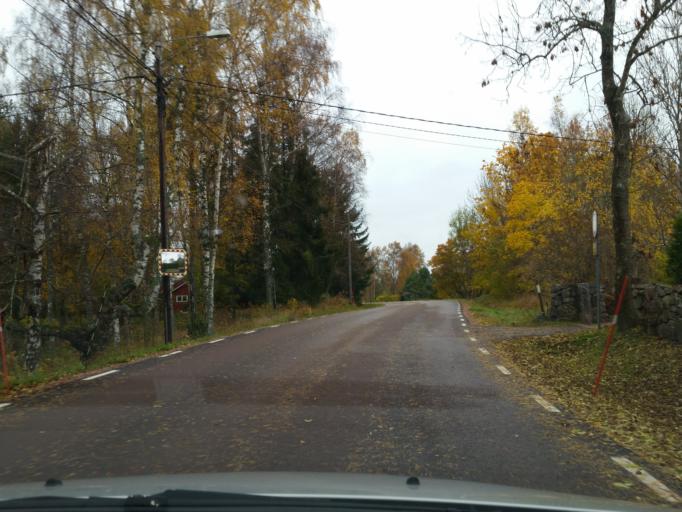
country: AX
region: Alands landsbygd
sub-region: Lemland
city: Lemland
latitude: 60.0750
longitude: 20.0832
